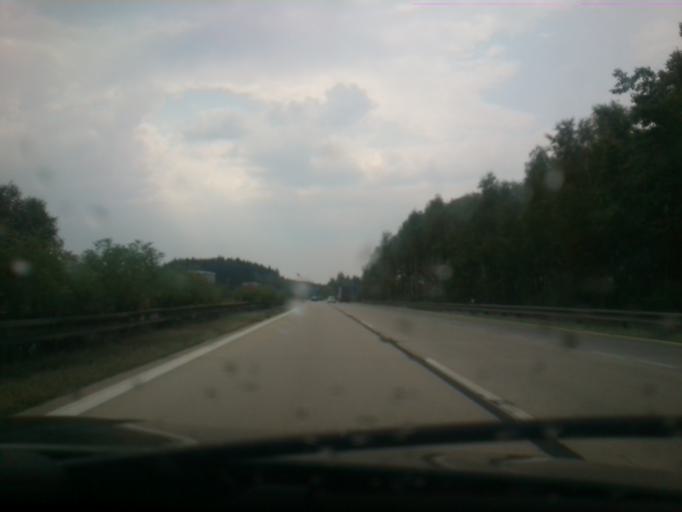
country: CZ
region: Vysocina
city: Merin
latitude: 49.4046
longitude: 15.8349
